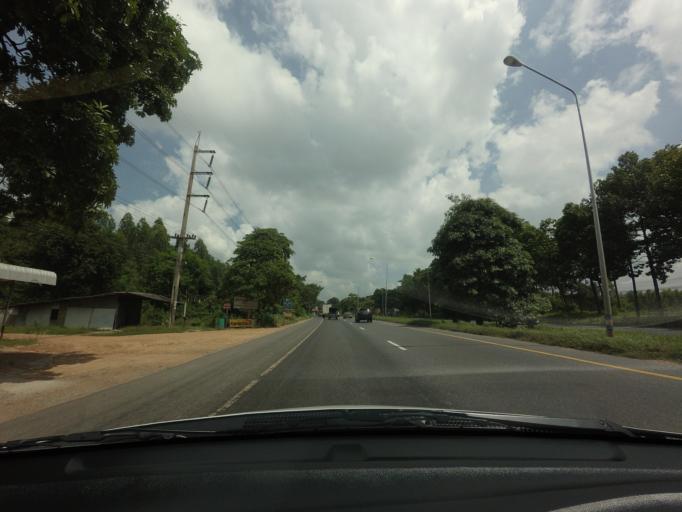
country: TH
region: Chachoengsao
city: Sanam Chai Khet
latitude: 13.7528
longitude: 101.5001
